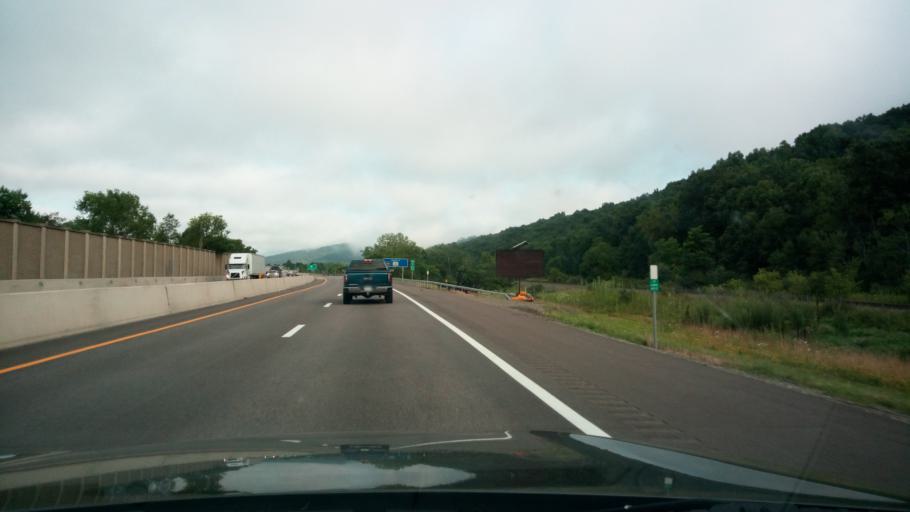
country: US
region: New York
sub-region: Steuben County
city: Corning
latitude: 42.1515
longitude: -77.0431
